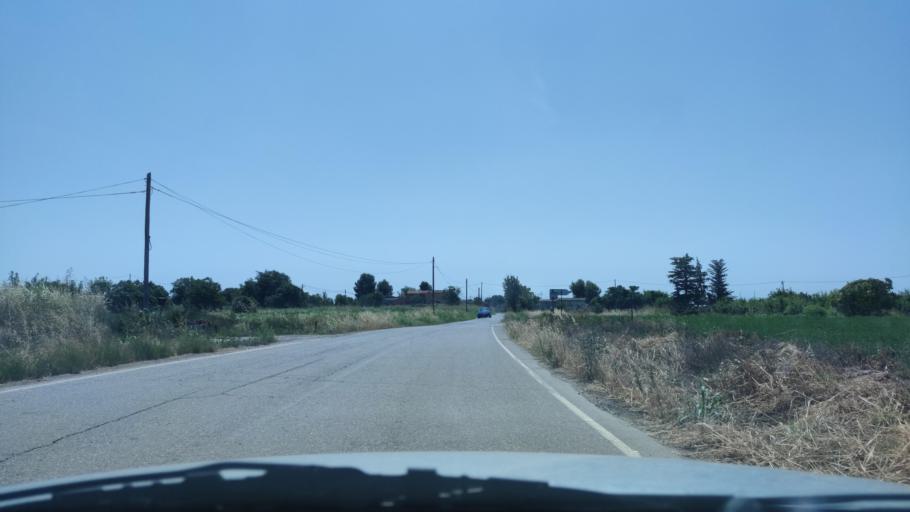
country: ES
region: Catalonia
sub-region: Provincia de Lleida
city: Alpicat
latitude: 41.6522
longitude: 0.5775
